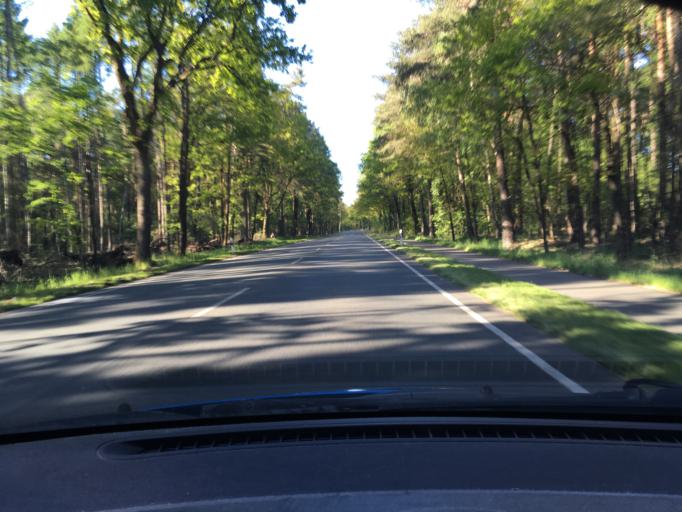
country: DE
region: Lower Saxony
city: Soltau
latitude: 53.0460
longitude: 9.8569
